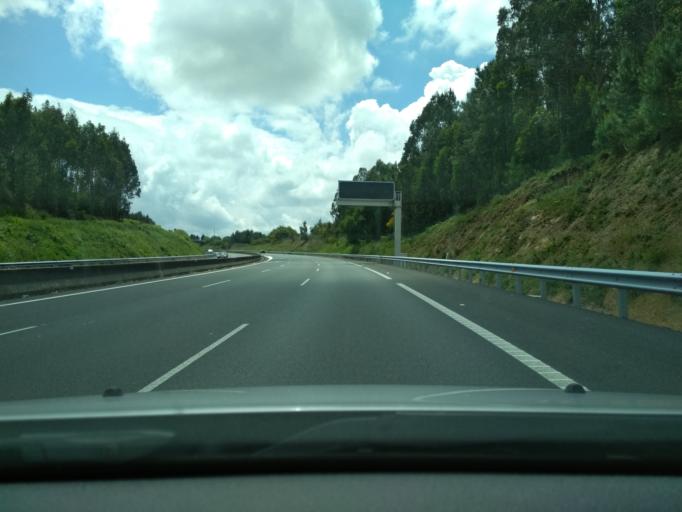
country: ES
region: Galicia
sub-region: Provincia de Pontevedra
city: Barro
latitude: 42.5278
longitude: -8.6706
